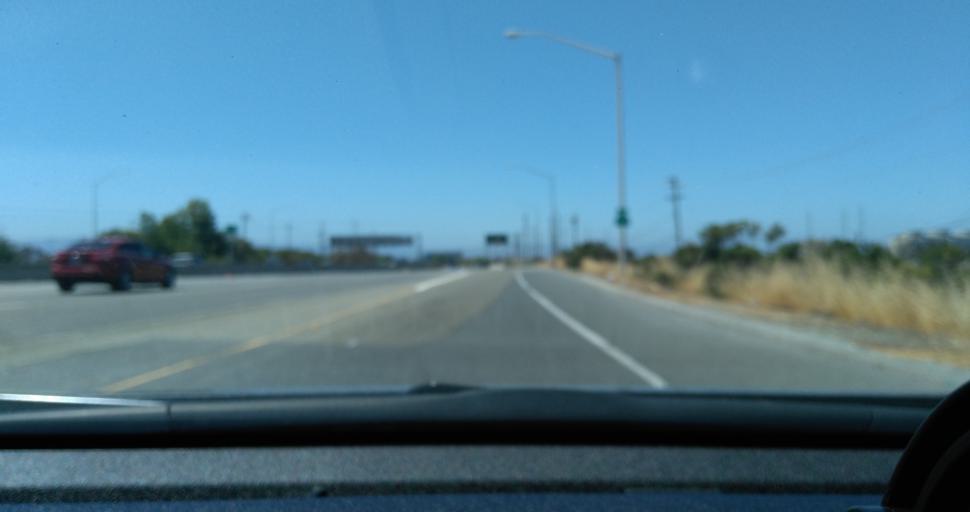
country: US
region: California
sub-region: Santa Clara County
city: Milpitas
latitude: 37.4228
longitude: -121.9281
